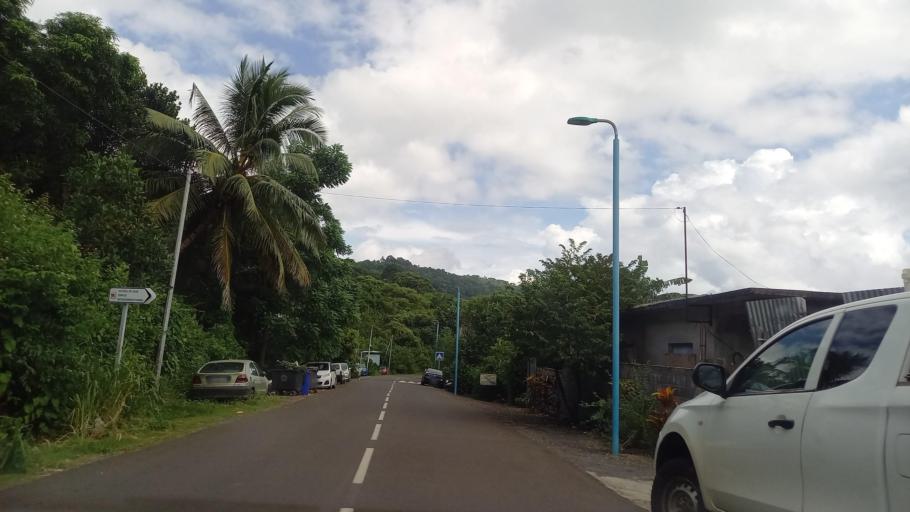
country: YT
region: Kani-Keli
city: Kani Keli
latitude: -12.9447
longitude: 45.1020
